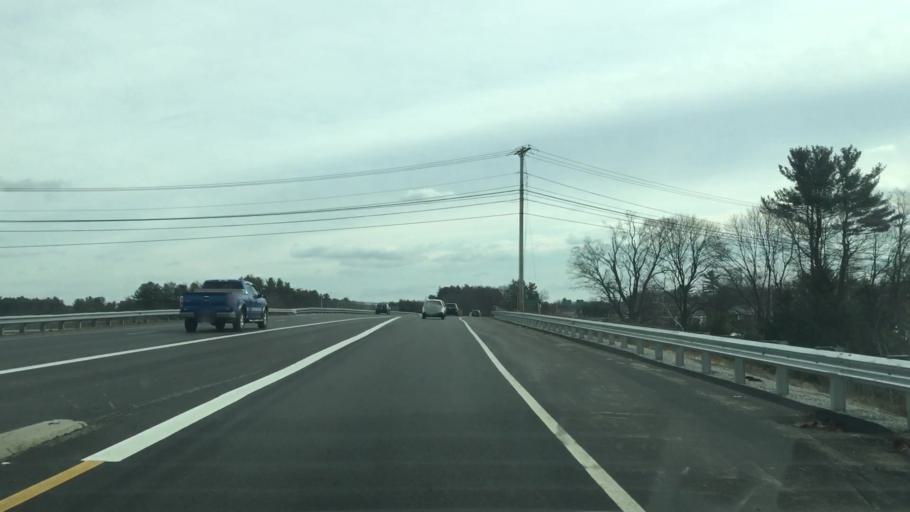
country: US
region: New Hampshire
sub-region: Hillsborough County
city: Bedford
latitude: 42.9514
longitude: -71.4790
